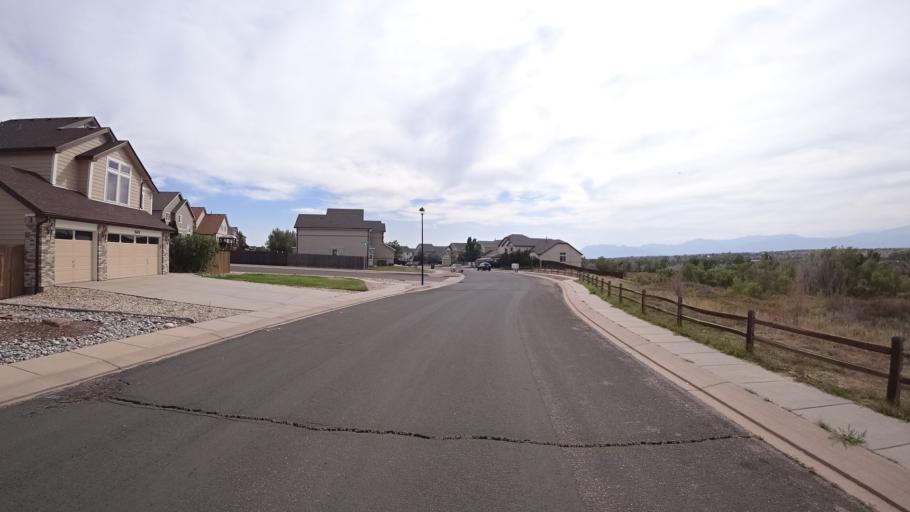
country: US
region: Colorado
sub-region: El Paso County
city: Cimarron Hills
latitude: 38.9108
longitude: -104.7010
